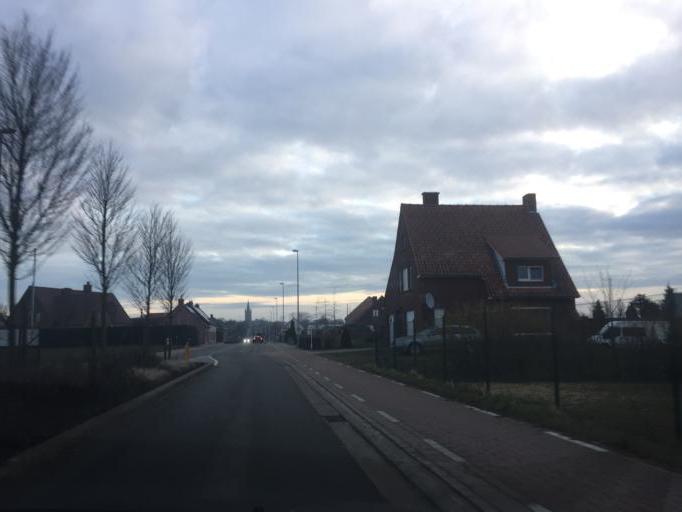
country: BE
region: Flanders
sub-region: Provincie West-Vlaanderen
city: Hooglede
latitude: 50.9714
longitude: 3.0719
